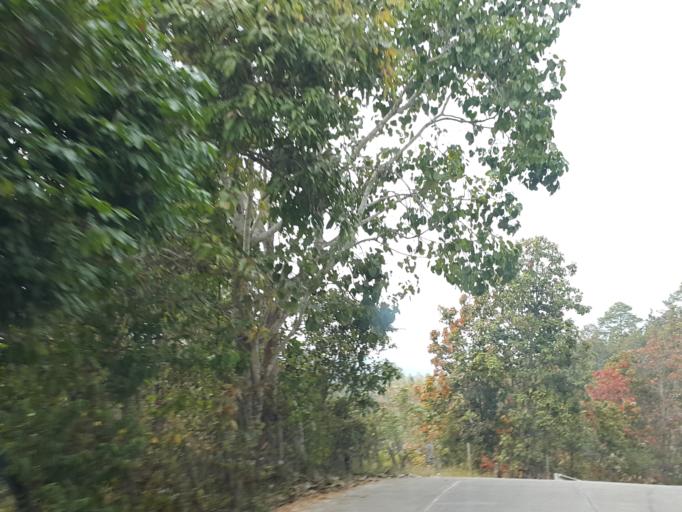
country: TH
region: Chiang Mai
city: Om Koi
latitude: 17.7976
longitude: 98.3524
